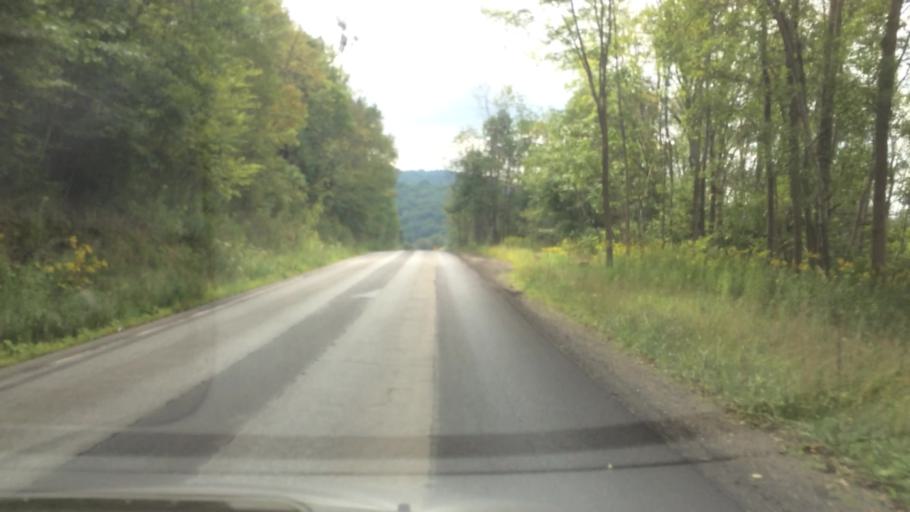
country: US
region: Pennsylvania
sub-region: McKean County
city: Bradford
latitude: 41.9174
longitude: -78.6435
